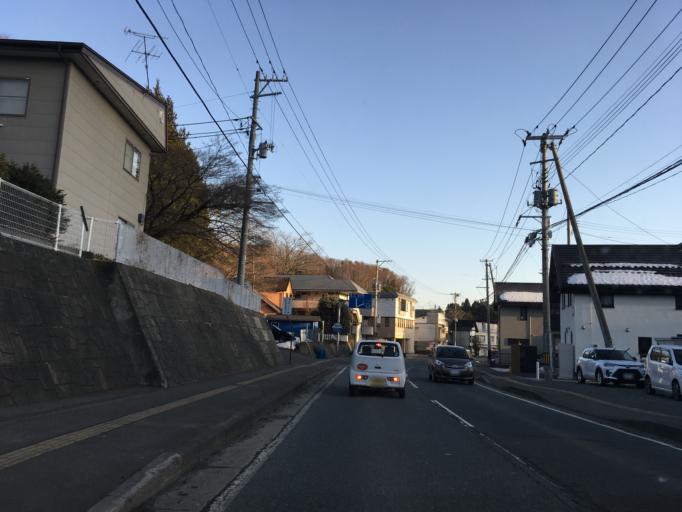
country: JP
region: Iwate
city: Morioka-shi
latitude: 39.7164
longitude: 141.1555
